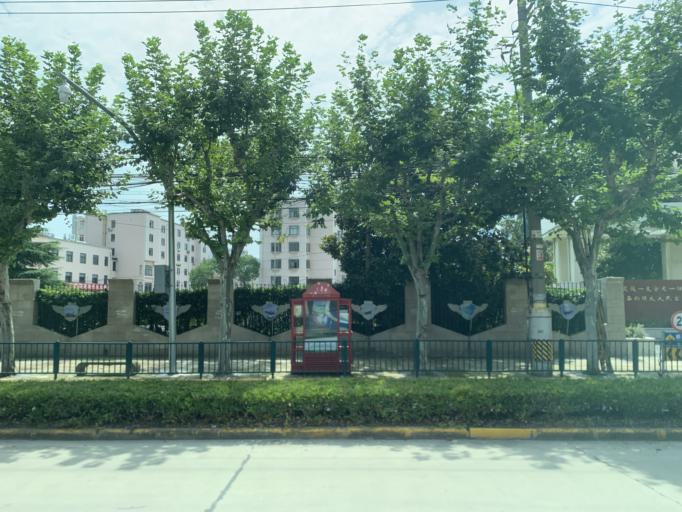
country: CN
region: Shanghai Shi
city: Pudong
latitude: 31.2396
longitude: 121.5269
